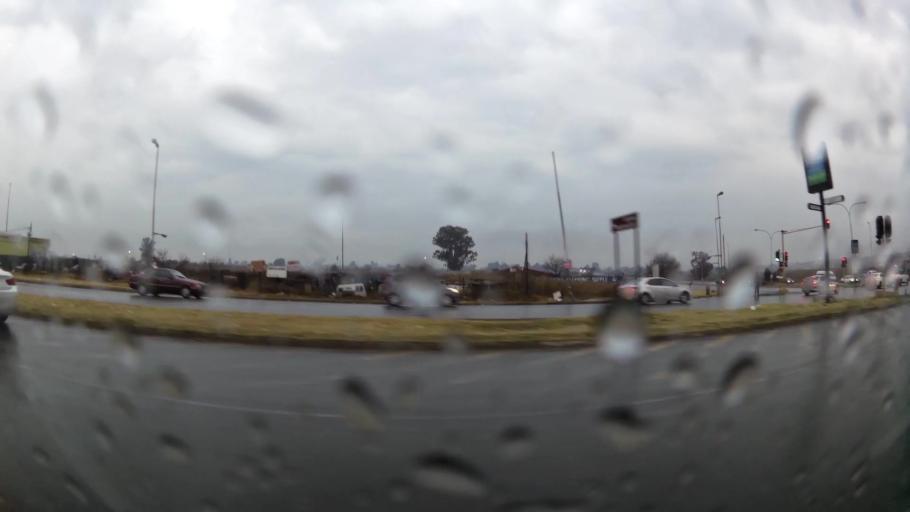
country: ZA
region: Gauteng
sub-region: City of Johannesburg Metropolitan Municipality
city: Soweto
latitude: -26.2623
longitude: 27.8906
